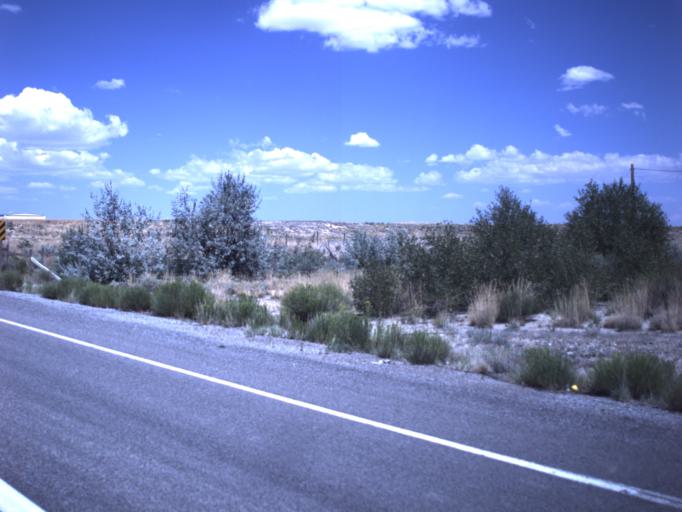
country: US
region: Utah
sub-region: Emery County
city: Huntington
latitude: 39.3603
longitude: -110.9261
